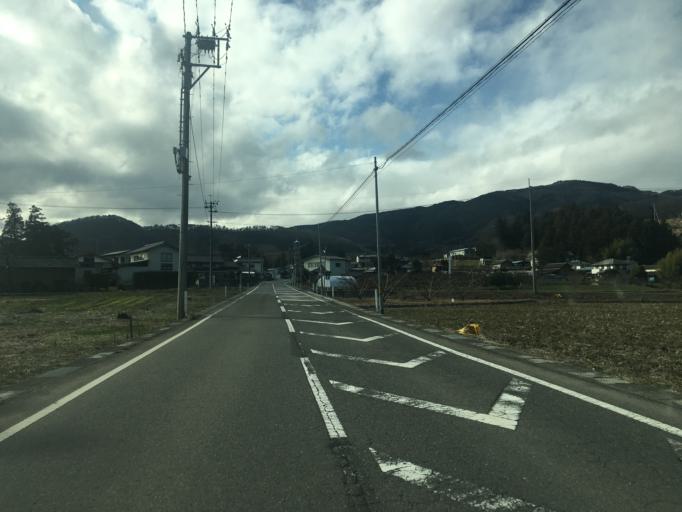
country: JP
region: Fukushima
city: Yanagawamachi-saiwaicho
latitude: 37.8925
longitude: 140.5853
